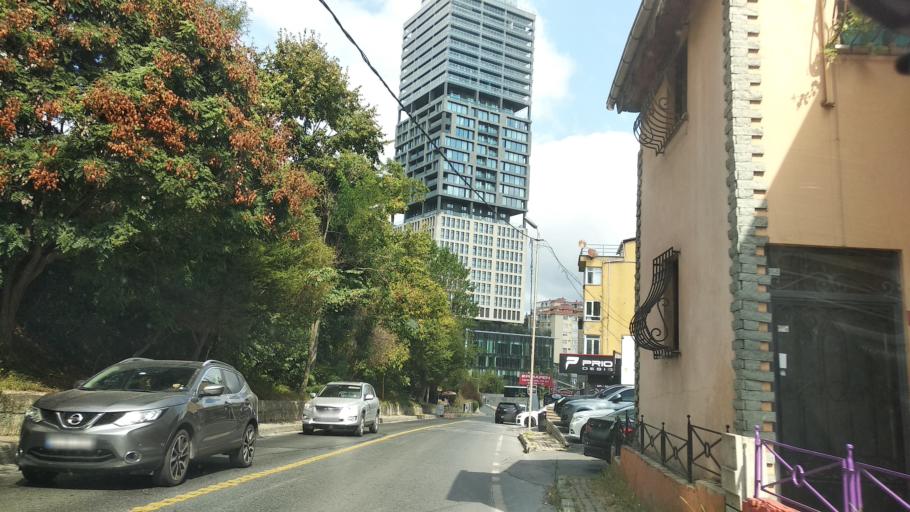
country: TR
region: Istanbul
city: Sisli
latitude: 41.0873
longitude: 29.0356
